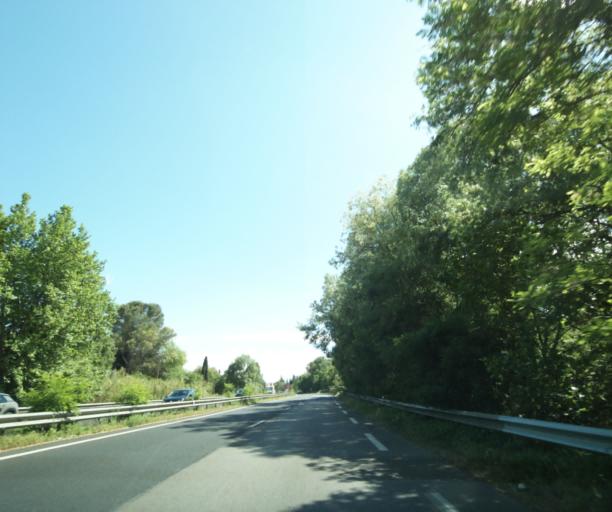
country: FR
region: Languedoc-Roussillon
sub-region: Departement de l'Herault
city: Laverune
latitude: 43.5976
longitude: 3.8200
